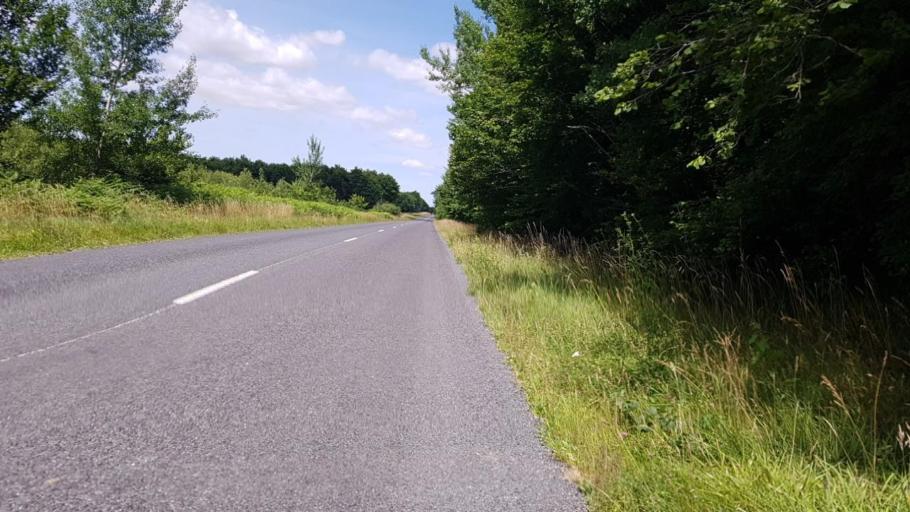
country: FR
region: Picardie
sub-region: Departement de l'Oise
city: Carlepont
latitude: 49.5237
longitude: 2.9836
